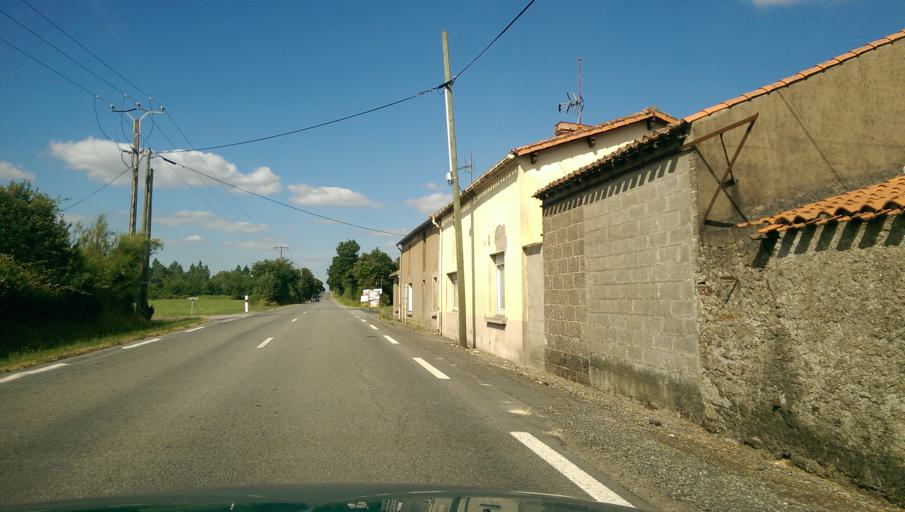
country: FR
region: Pays de la Loire
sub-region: Departement de la Loire-Atlantique
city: Lege
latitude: 46.9065
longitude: -1.5609
